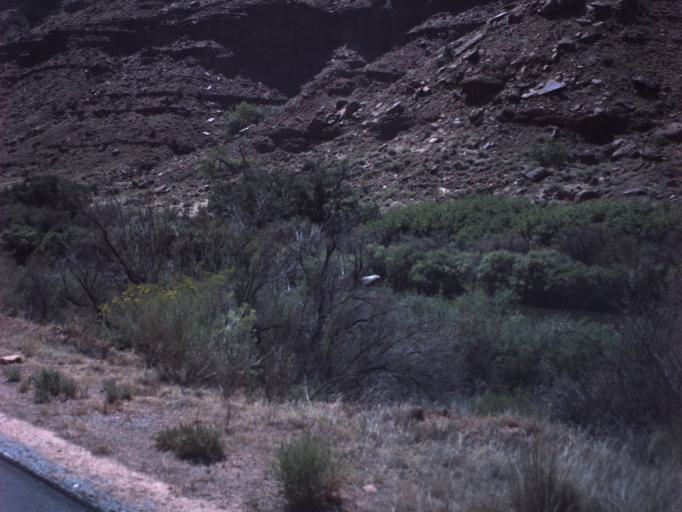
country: US
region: Utah
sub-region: Grand County
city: Moab
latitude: 38.6474
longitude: -109.5052
